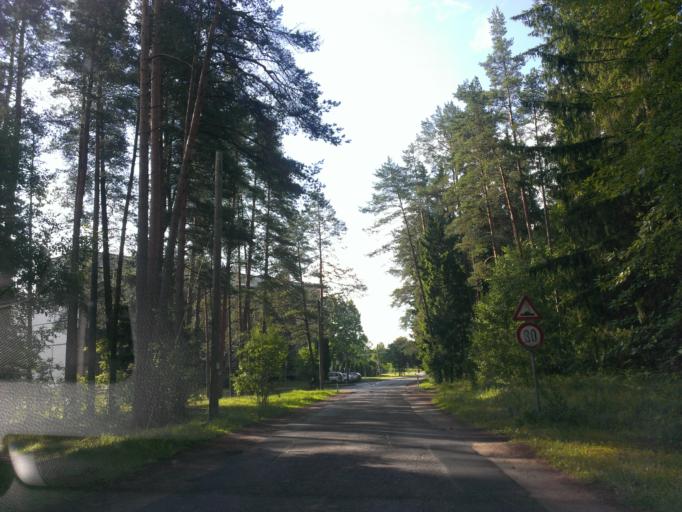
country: LV
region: Incukalns
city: Vangazi
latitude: 57.0956
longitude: 24.5390
